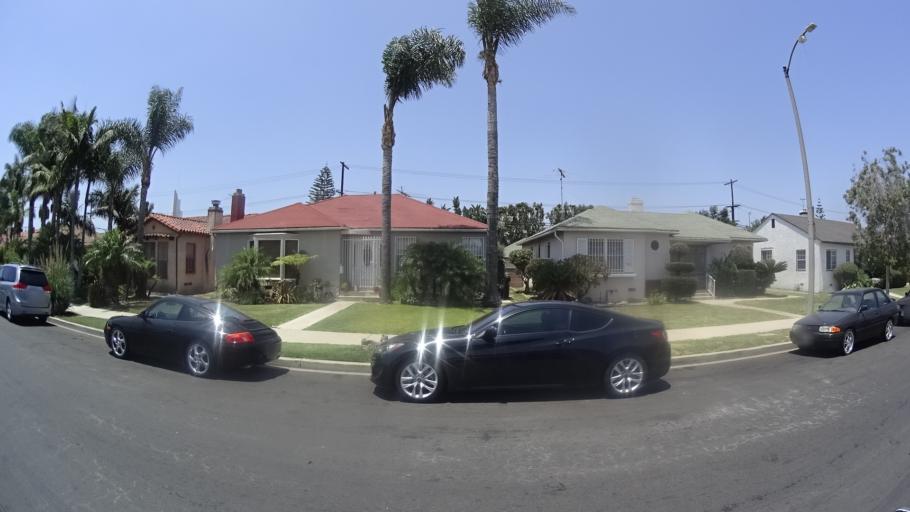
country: US
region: California
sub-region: Los Angeles County
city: View Park-Windsor Hills
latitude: 34.0119
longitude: -118.3337
